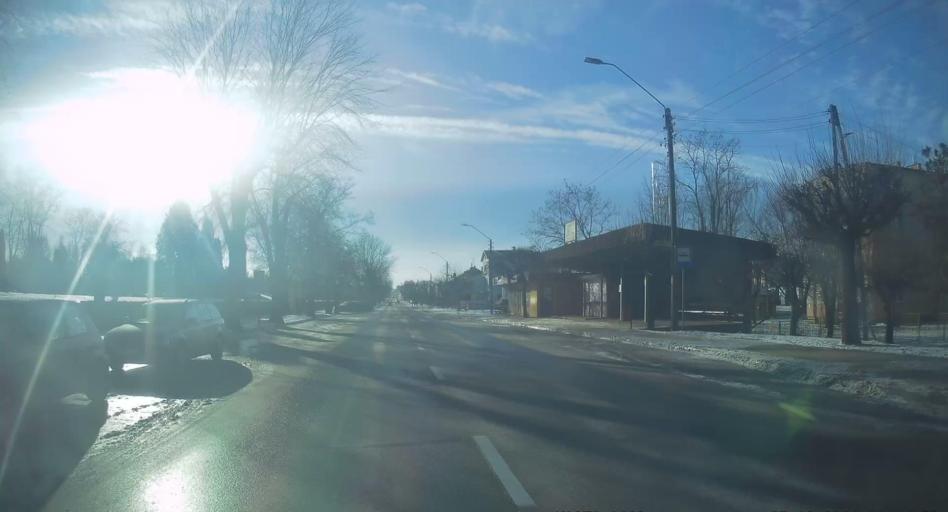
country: PL
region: Lodz Voivodeship
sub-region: Powiat rawski
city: Rawa Mazowiecka
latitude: 51.7583
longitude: 20.2448
